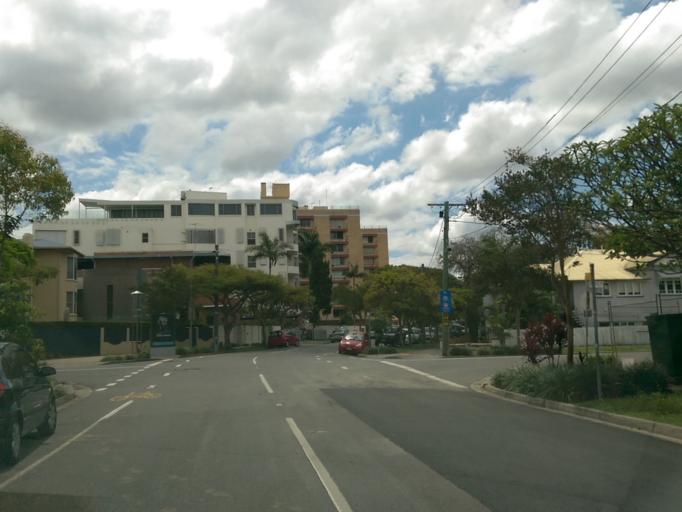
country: AU
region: Queensland
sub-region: Brisbane
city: Woolloongabba
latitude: -27.4741
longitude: 153.0430
